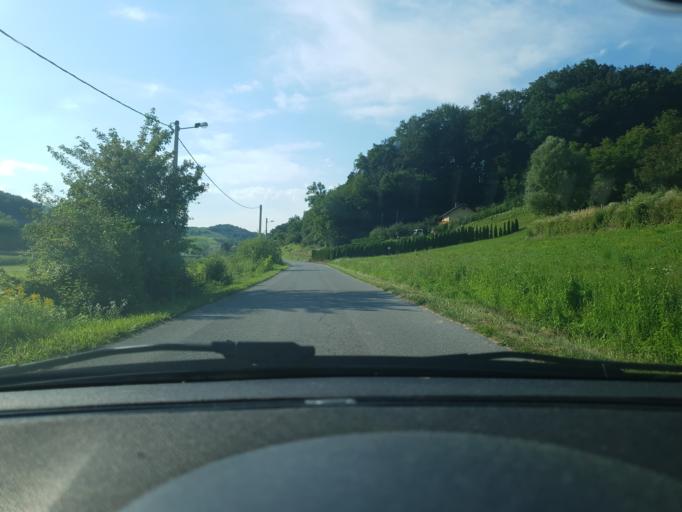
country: HR
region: Krapinsko-Zagorska
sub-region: Grad Krapina
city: Krapina
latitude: 46.1350
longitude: 15.8559
